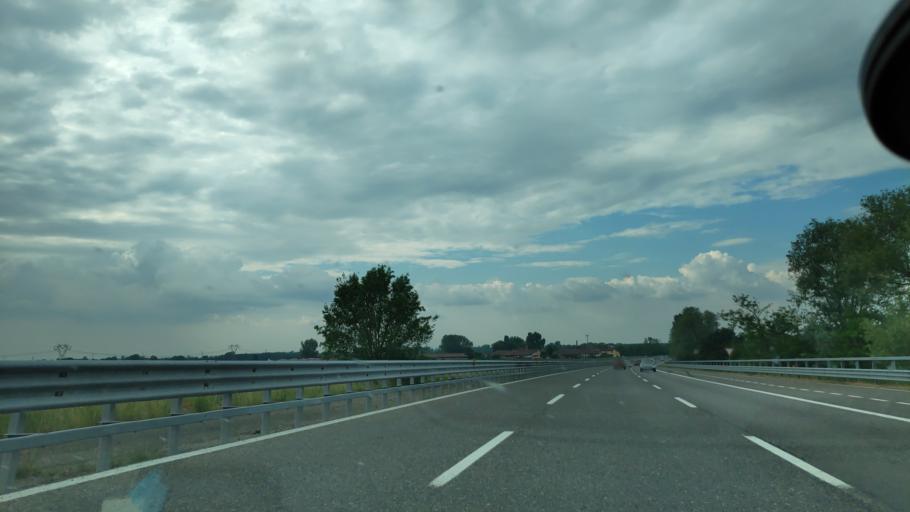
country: IT
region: Lombardy
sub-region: Provincia di Pavia
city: Pieve Albignola
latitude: 45.0896
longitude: 8.9696
